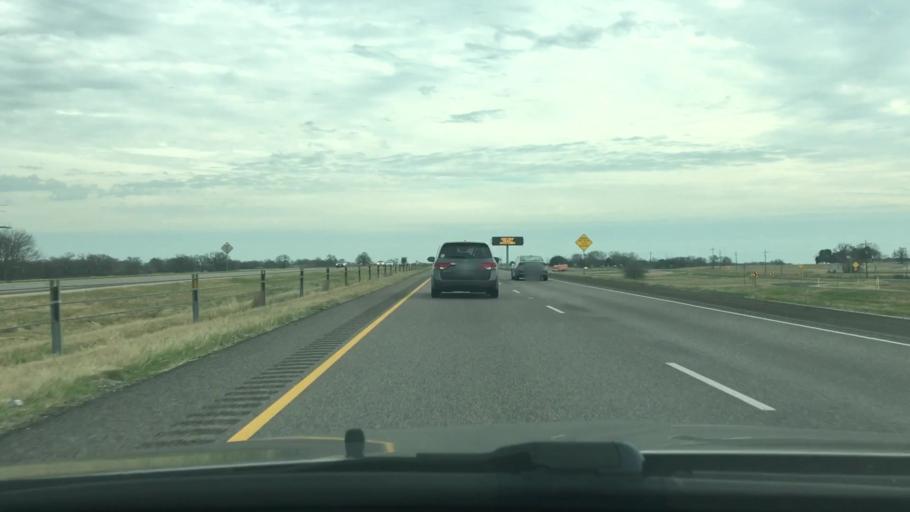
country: US
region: Texas
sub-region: Madison County
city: Madisonville
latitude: 31.0167
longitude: -95.9248
